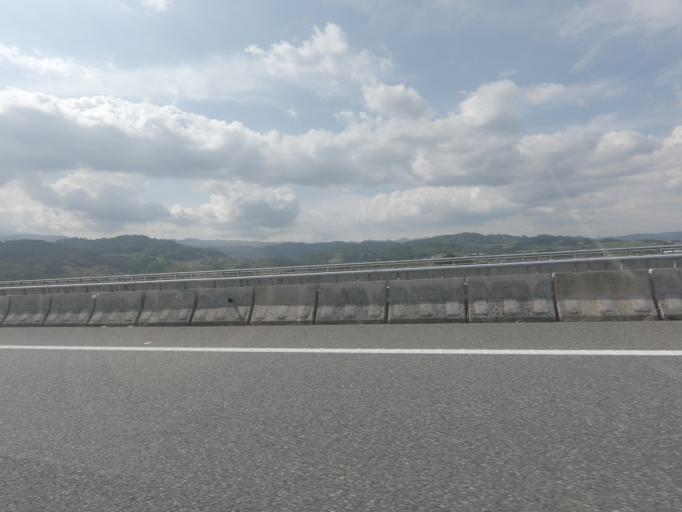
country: ES
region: Galicia
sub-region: Provincia de Ourense
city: Ribadavia
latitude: 42.3030
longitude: -8.1277
